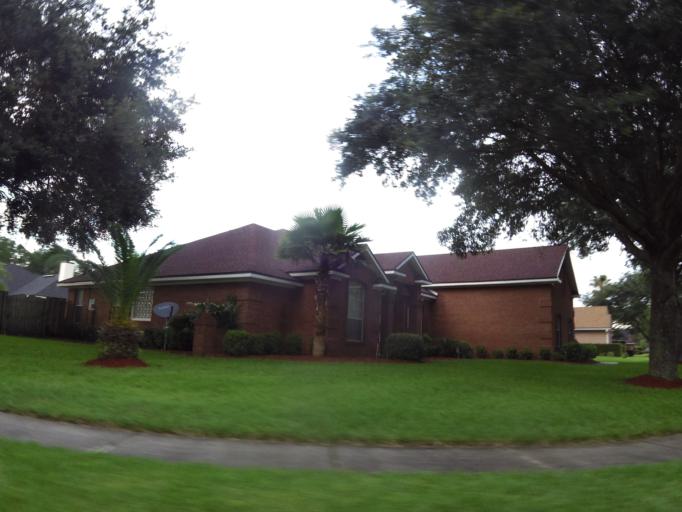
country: US
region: Florida
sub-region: Duval County
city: Baldwin
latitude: 30.3063
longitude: -81.8280
